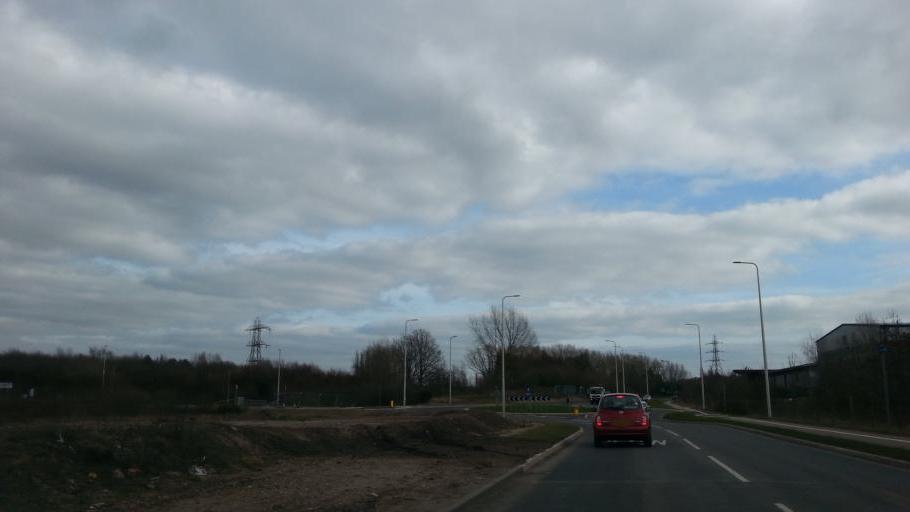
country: GB
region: England
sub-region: Staffordshire
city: Rugeley
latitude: 52.7523
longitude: -1.9165
